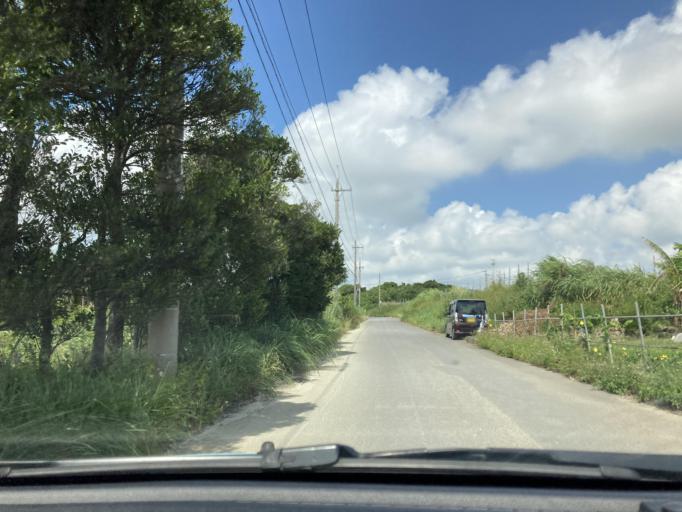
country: JP
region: Okinawa
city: Itoman
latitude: 26.1024
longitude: 127.7266
